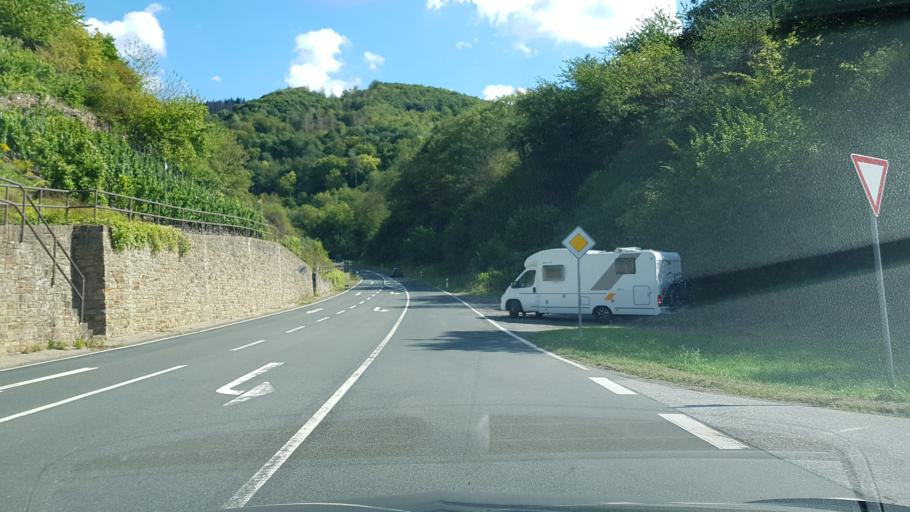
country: DE
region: Rheinland-Pfalz
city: Bruttig-Fankel
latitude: 50.1374
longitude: 7.2381
